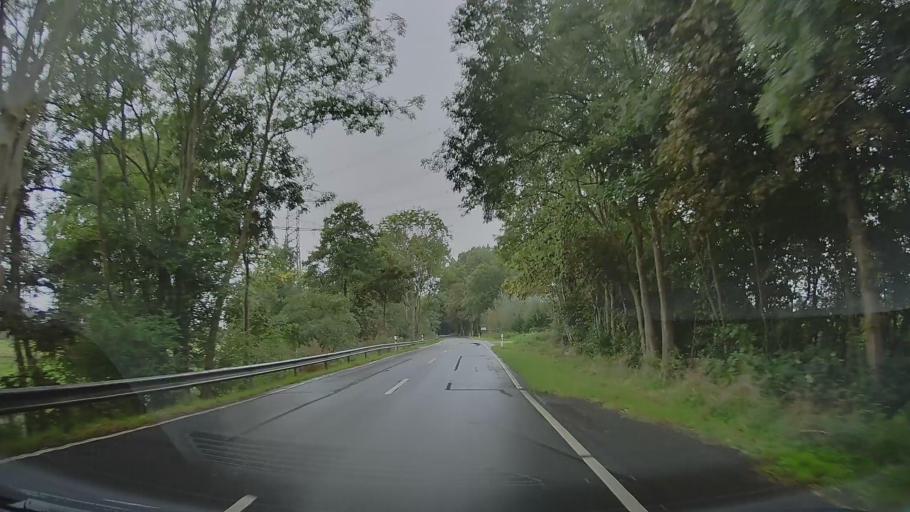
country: DE
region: Schleswig-Holstein
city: Buttel
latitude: 53.8973
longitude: 9.2150
